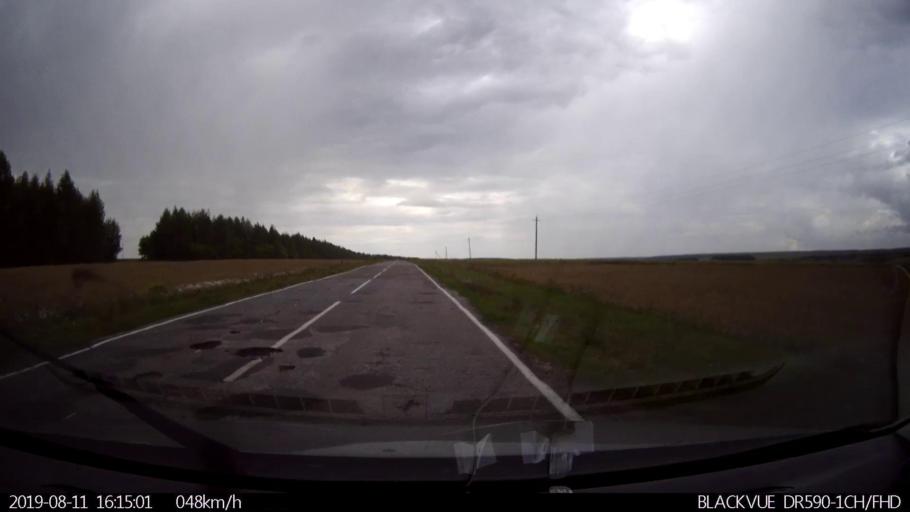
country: RU
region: Ulyanovsk
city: Mayna
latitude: 54.0320
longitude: 47.6306
